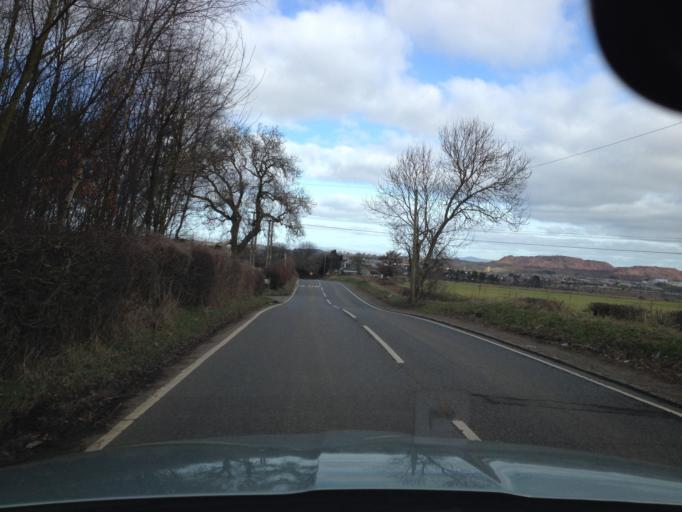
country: GB
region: Scotland
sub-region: West Lothian
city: Broxburn
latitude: 55.9185
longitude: -3.4617
